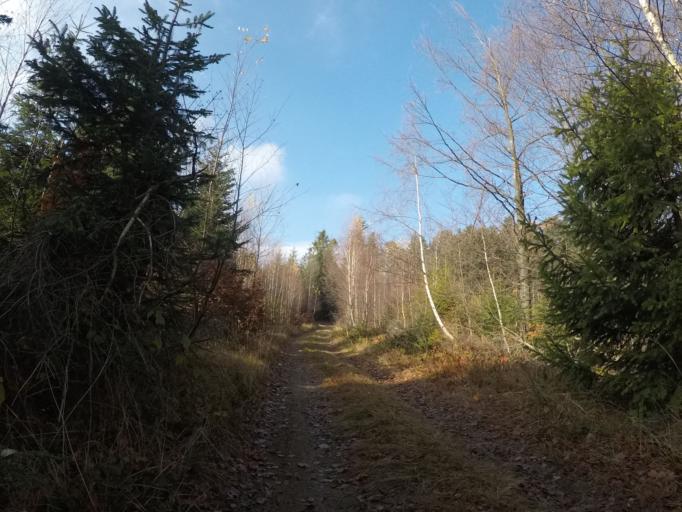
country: SK
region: Kosicky
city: Gelnica
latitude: 48.7646
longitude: 21.0646
